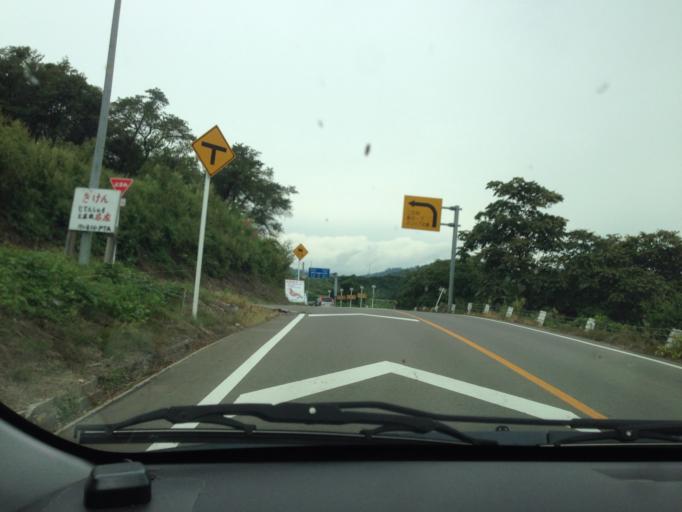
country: JP
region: Fukushima
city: Kitakata
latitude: 37.6105
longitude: 139.8017
